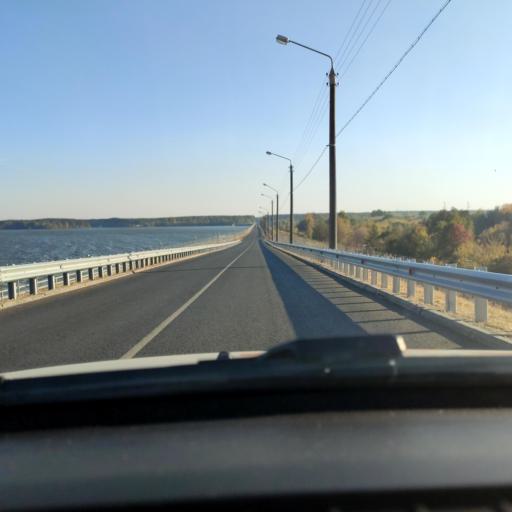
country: RU
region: Voronezj
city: Shilovo
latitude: 51.5497
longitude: 39.1351
